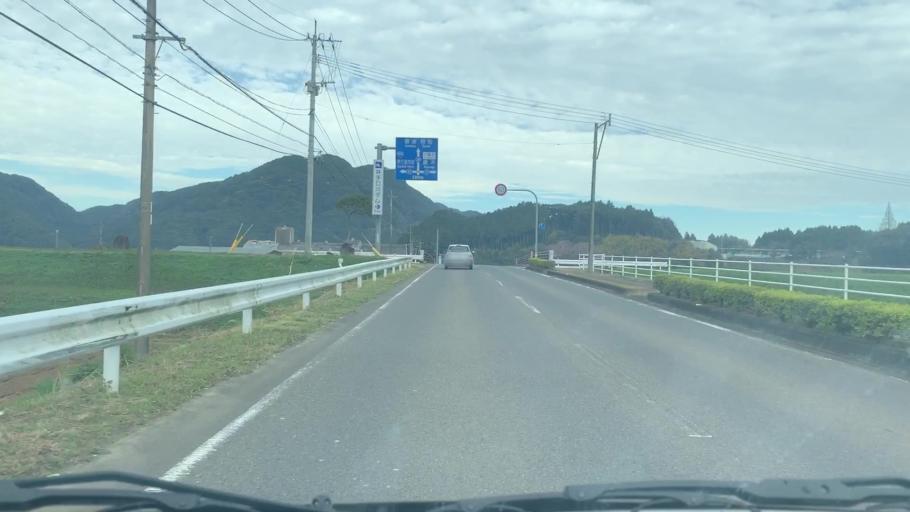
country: JP
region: Saga Prefecture
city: Imaricho-ko
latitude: 33.2988
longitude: 129.9700
